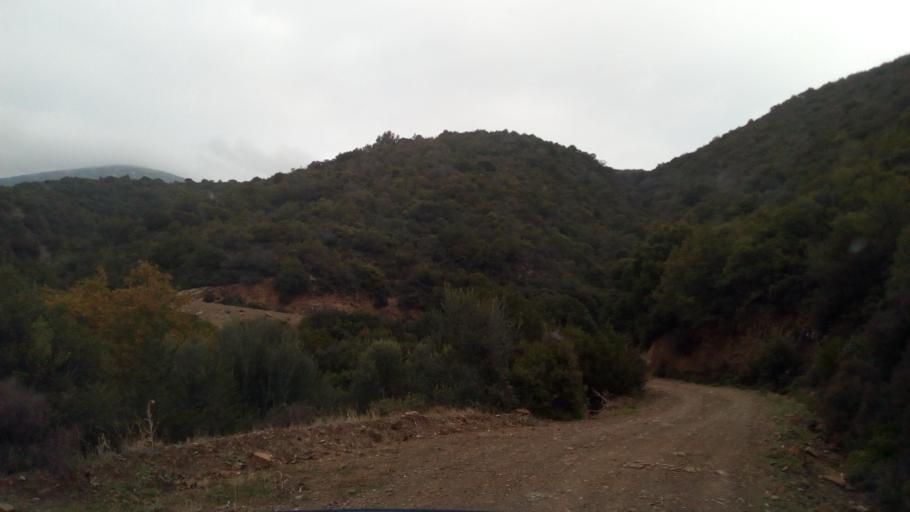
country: GR
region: West Greece
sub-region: Nomos Achaias
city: Temeni
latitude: 38.3688
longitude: 22.1586
